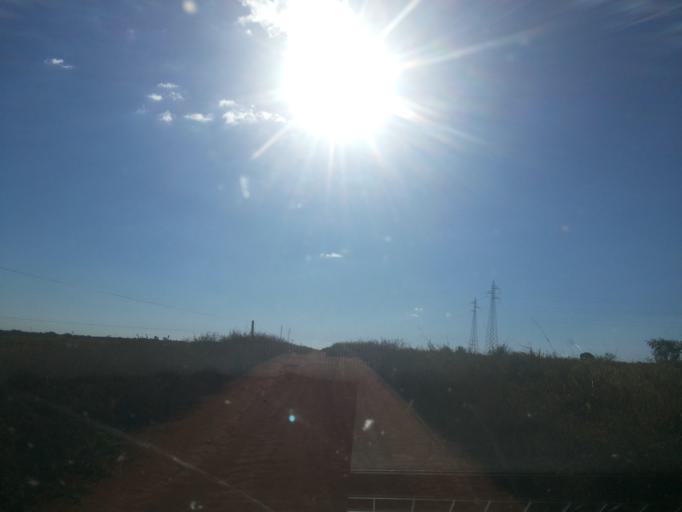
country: BR
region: Minas Gerais
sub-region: Centralina
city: Centralina
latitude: -18.7361
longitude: -49.1605
